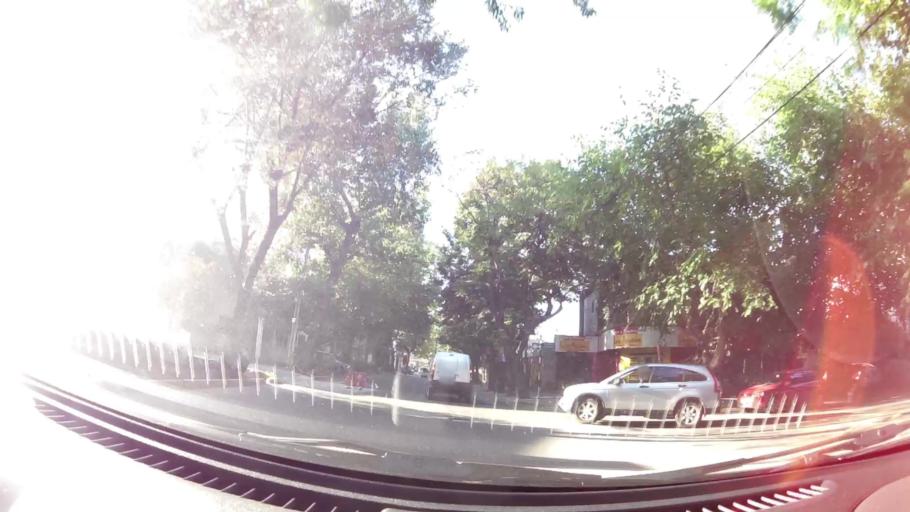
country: AR
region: Mendoza
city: Mendoza
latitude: -32.9041
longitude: -68.8517
